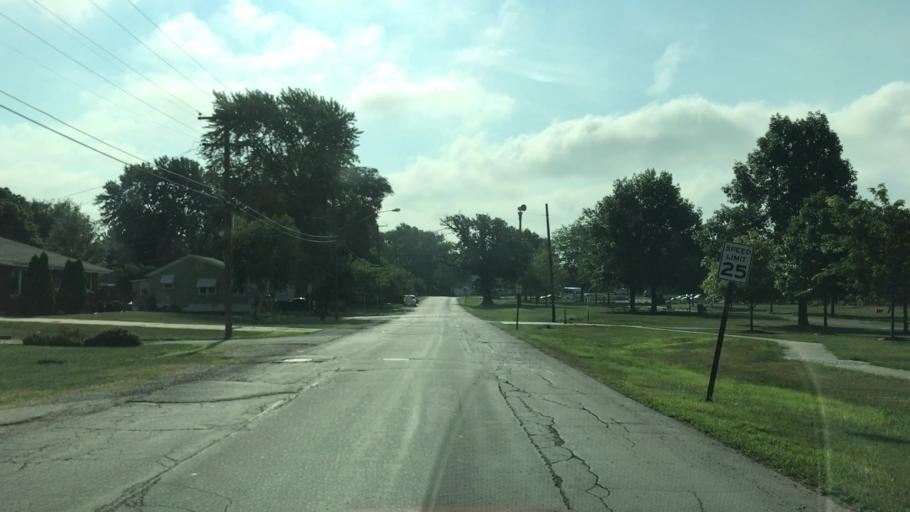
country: US
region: Illinois
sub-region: Will County
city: Lockport
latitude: 41.5787
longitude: -88.0568
